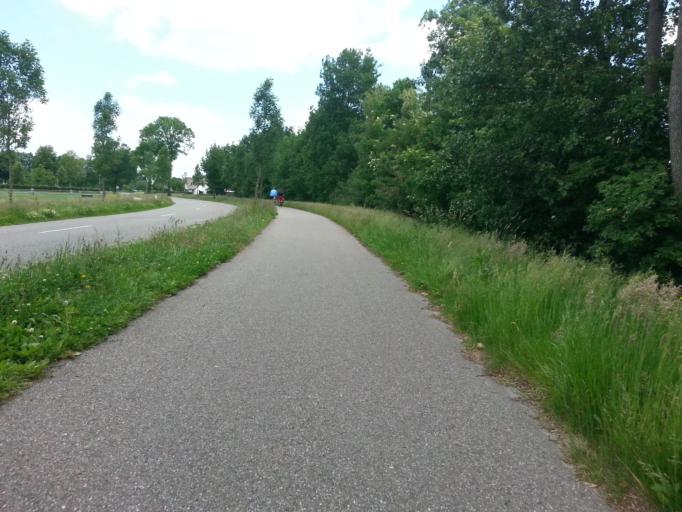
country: NL
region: Gelderland
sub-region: Gemeente Ede
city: Ederveen
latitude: 52.1037
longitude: 5.5484
